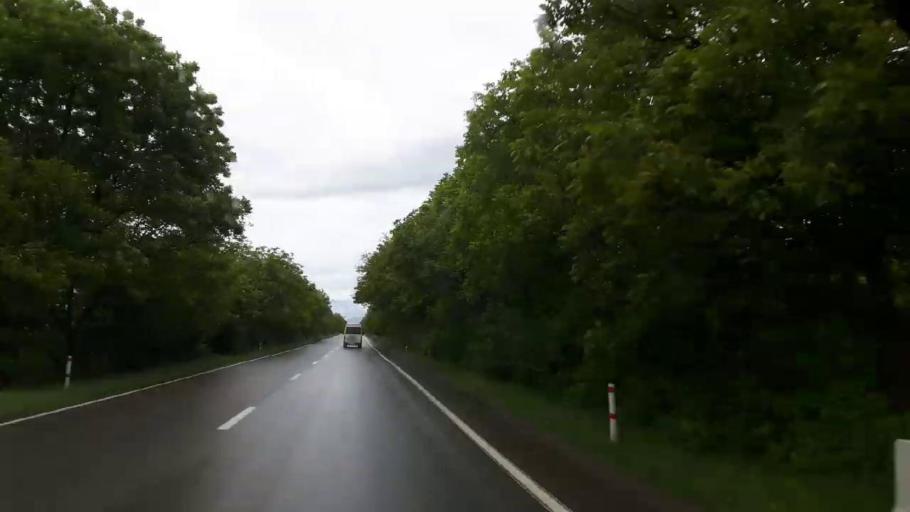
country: GE
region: Shida Kartli
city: Kaspi
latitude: 41.9579
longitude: 44.4851
